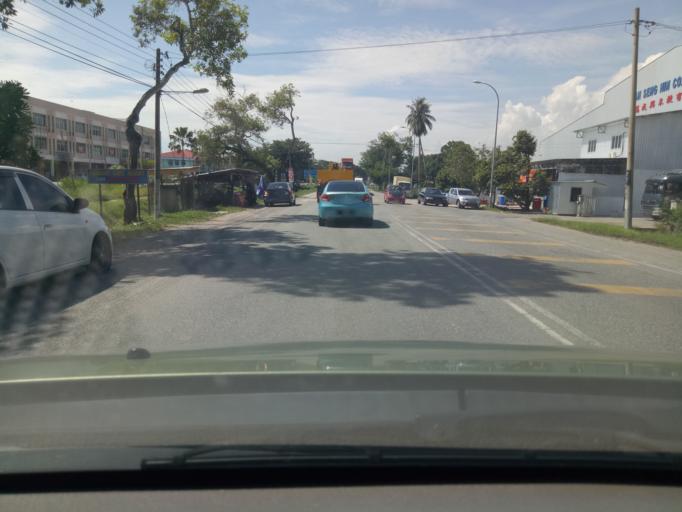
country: MY
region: Kedah
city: Alor Setar
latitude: 5.9709
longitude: 100.4012
